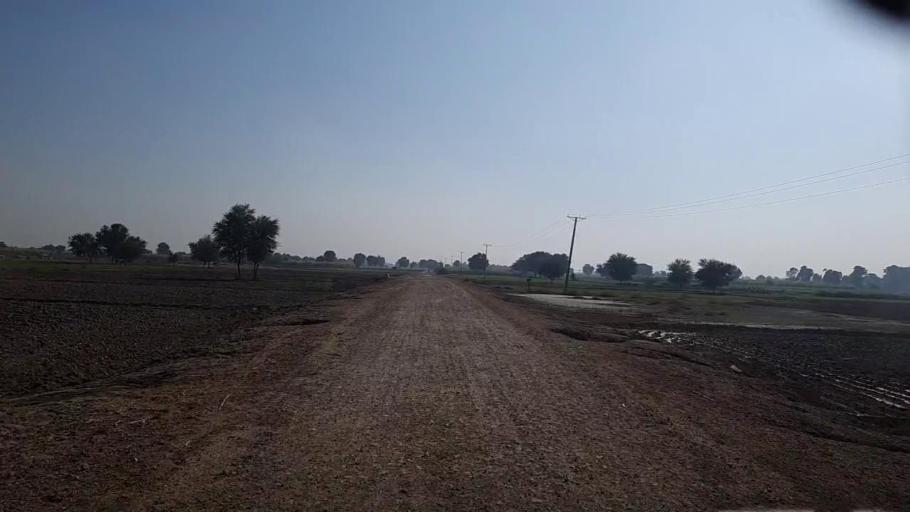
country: PK
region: Sindh
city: Darya Khan Marri
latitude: 26.6623
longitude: 68.3363
